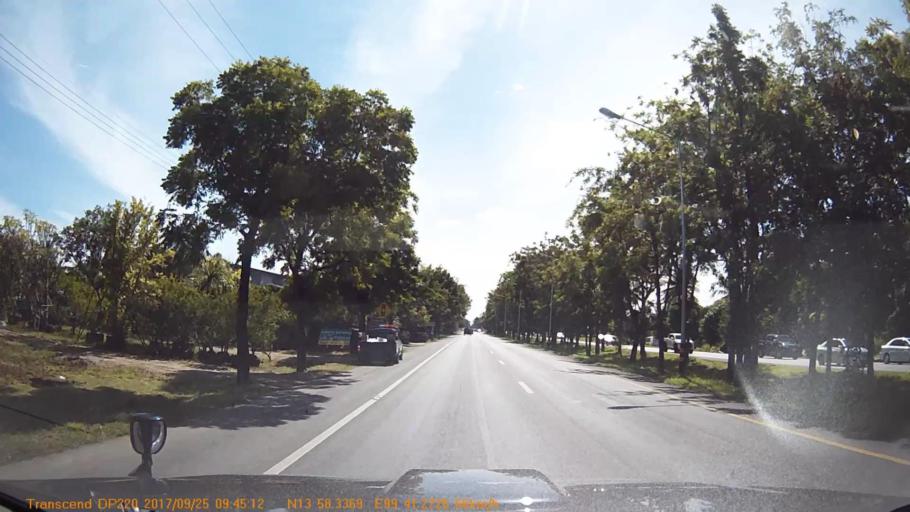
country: TH
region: Kanchanaburi
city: Tha Muang
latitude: 13.9722
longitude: 99.6882
